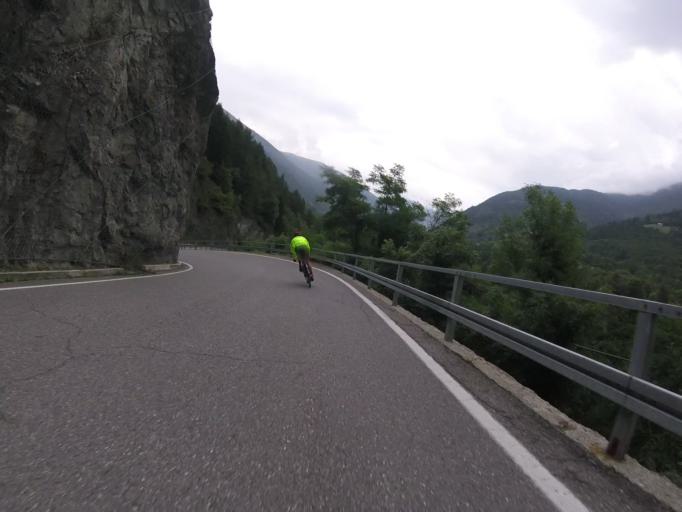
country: IT
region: Lombardy
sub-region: Provincia di Brescia
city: Monno
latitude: 46.2122
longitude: 10.3496
